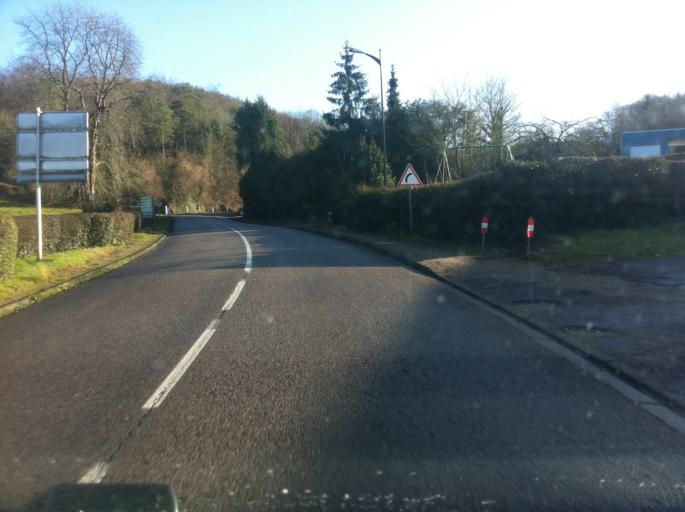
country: FR
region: Haute-Normandie
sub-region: Departement de la Seine-Maritime
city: Saint-Martin-de-Boscherville
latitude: 49.4487
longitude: 0.9693
